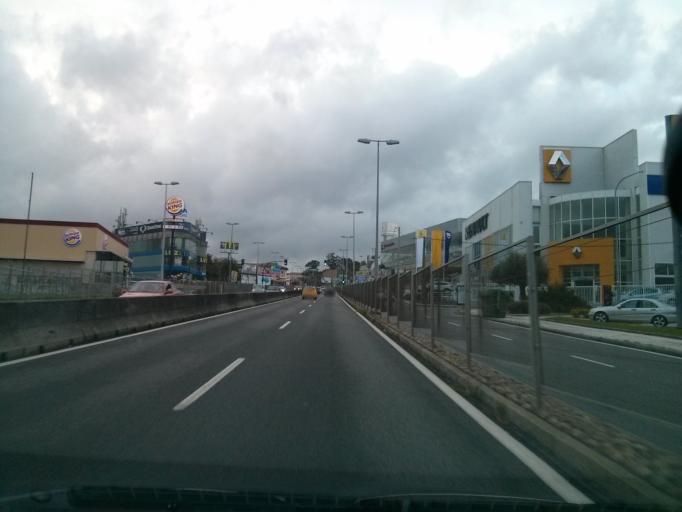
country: ES
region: Galicia
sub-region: Provincia de Pontevedra
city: Vigo
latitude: 42.2199
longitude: -8.7053
